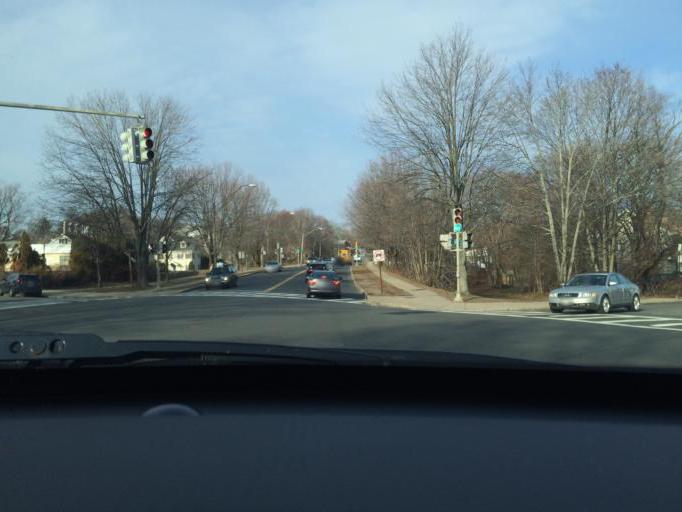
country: US
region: Massachusetts
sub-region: Suffolk County
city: Jamaica Plain
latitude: 42.2847
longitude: -71.1476
